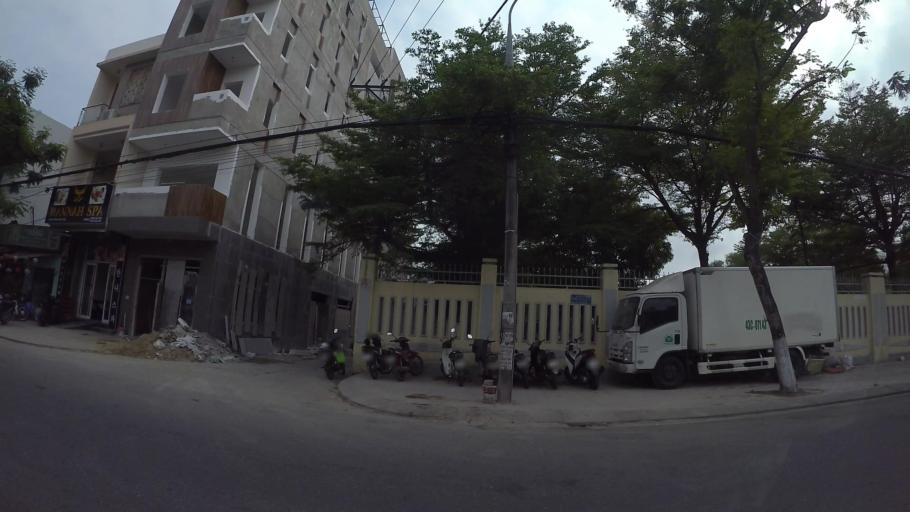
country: VN
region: Da Nang
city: Son Tra
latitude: 16.0660
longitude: 108.2382
